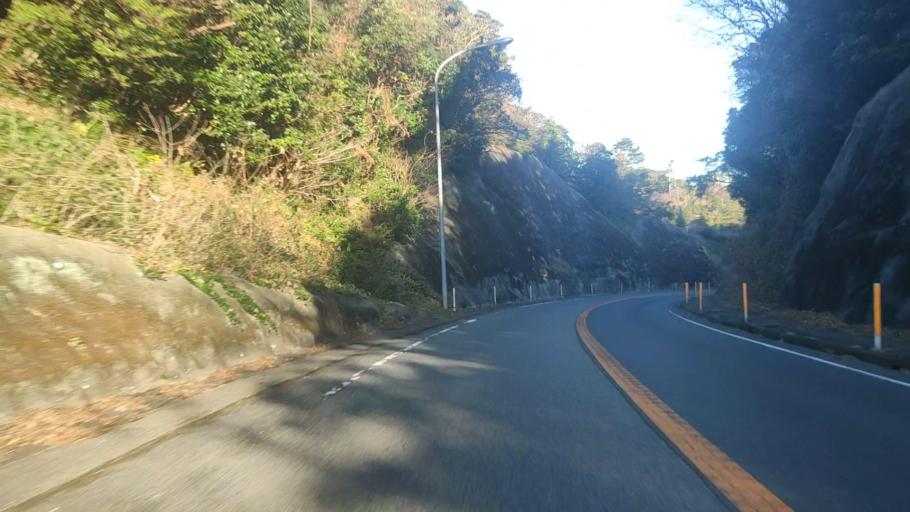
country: JP
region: Miyazaki
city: Nobeoka
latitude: 32.3471
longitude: 131.6228
